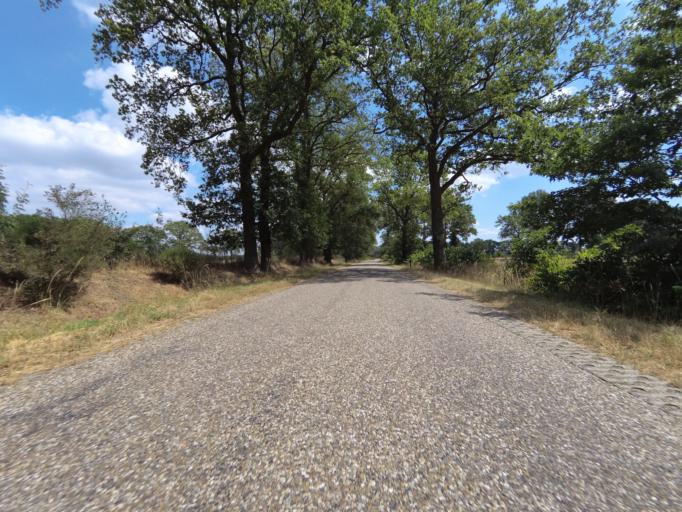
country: NL
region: Overijssel
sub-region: Gemeente Raalte
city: Raalte
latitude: 52.3203
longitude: 6.3807
